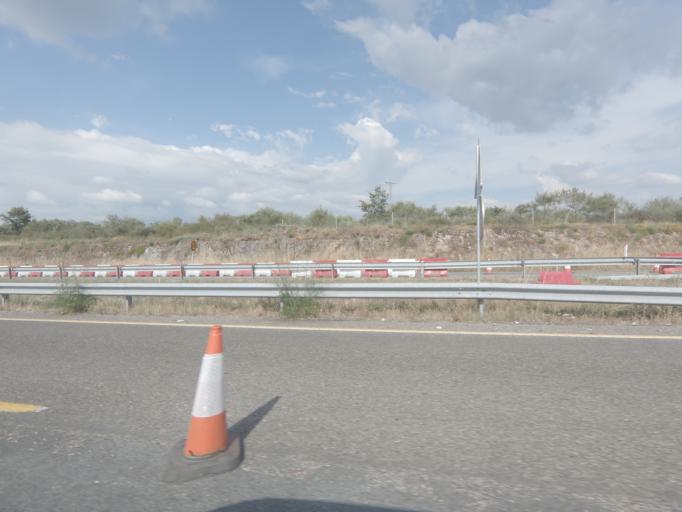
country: ES
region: Galicia
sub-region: Provincia de Ourense
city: Taboadela
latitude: 42.2410
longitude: -7.8593
